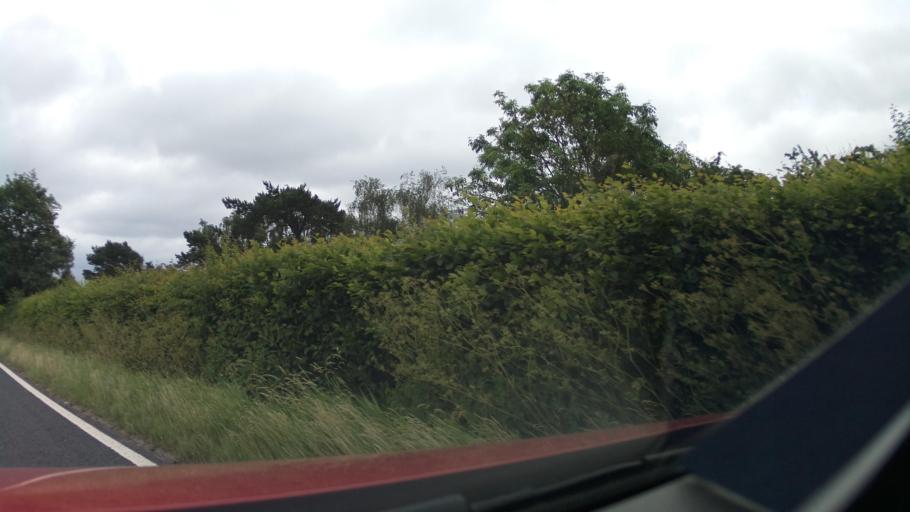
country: GB
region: England
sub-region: Leicestershire
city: Kirby Muxloe
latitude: 52.6645
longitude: -1.2268
